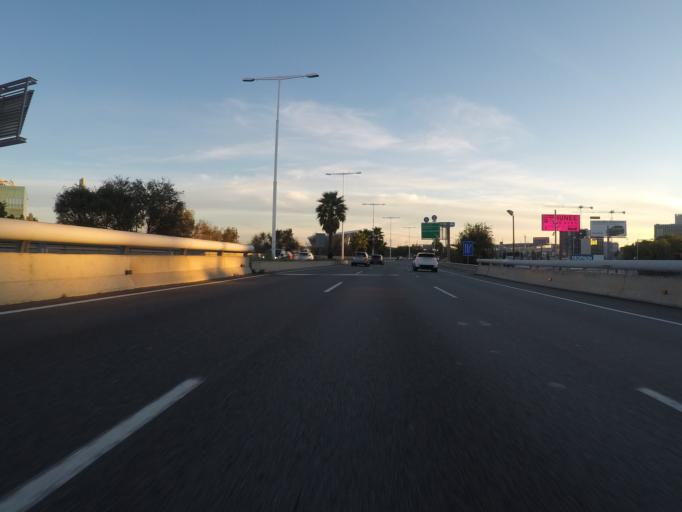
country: ES
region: Catalonia
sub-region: Provincia de Barcelona
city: Sant Adria de Besos
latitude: 41.4180
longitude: 2.2254
